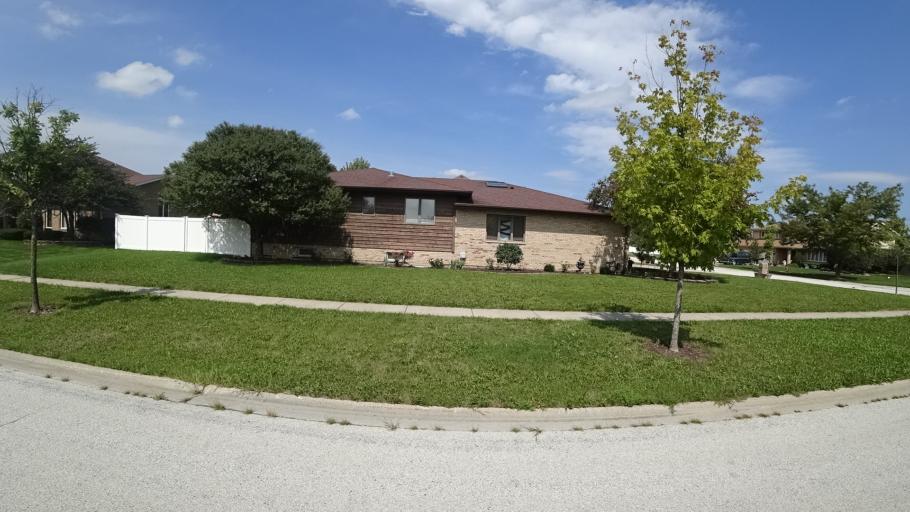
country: US
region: Illinois
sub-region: Cook County
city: Tinley Park
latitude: 41.5661
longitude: -87.8137
